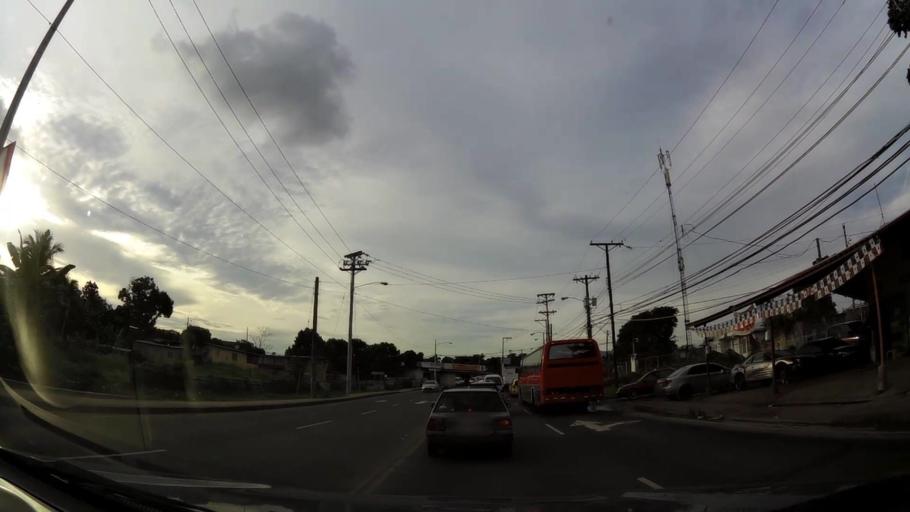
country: PA
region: Panama
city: Tocumen
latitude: 9.0967
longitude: -79.3698
